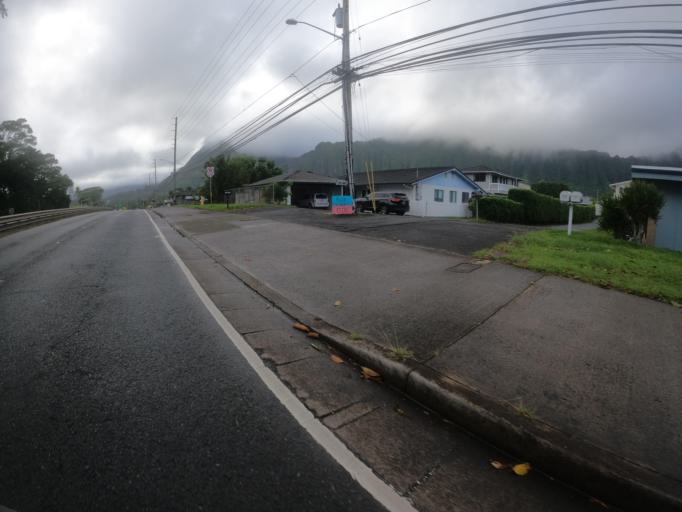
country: US
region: Hawaii
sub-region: Honolulu County
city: Kane'ohe
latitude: 21.3910
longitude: -157.7958
